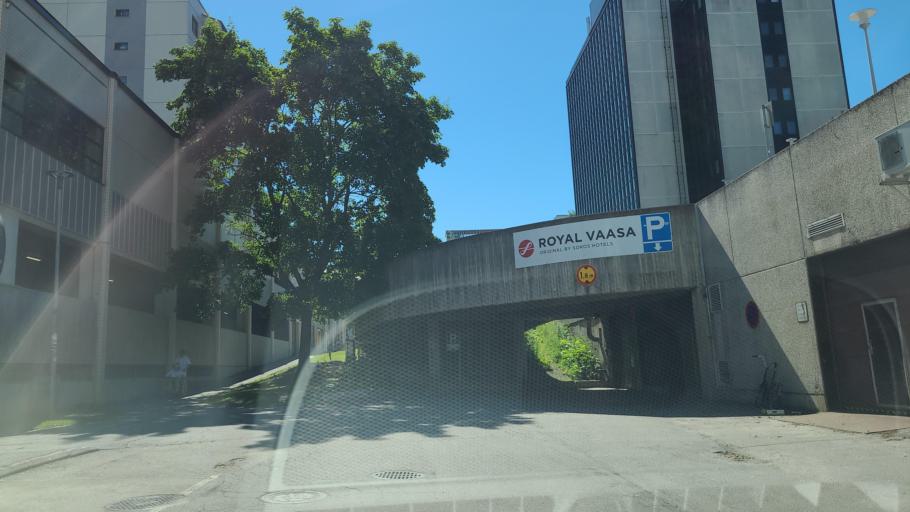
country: FI
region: Ostrobothnia
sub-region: Vaasa
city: Vaasa
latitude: 63.0968
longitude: 21.6201
